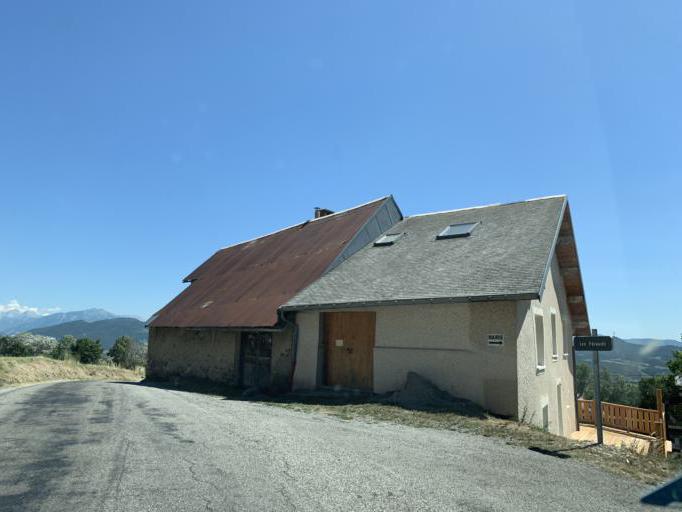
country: FR
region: Provence-Alpes-Cote d'Azur
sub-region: Departement des Hautes-Alpes
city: La Batie-Neuve
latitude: 44.5941
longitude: 6.1517
